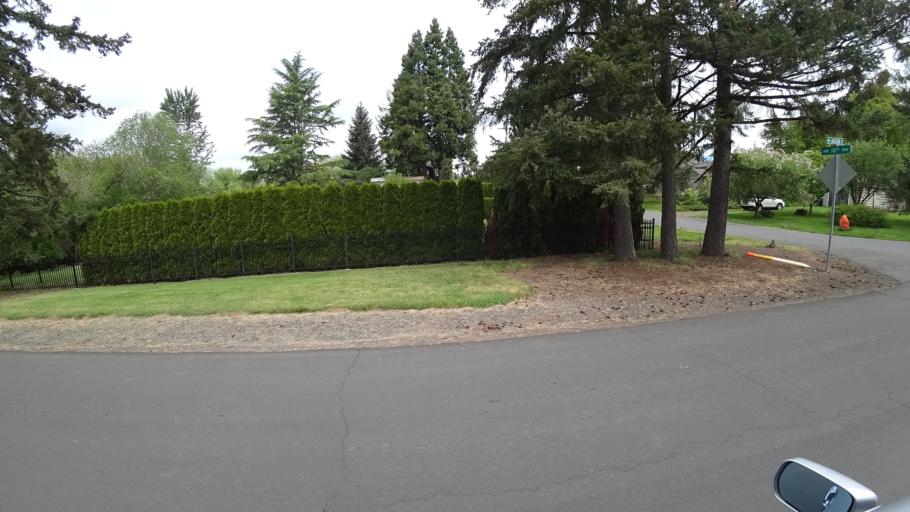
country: US
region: Oregon
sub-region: Washington County
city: Hillsboro
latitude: 45.5253
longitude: -123.0037
